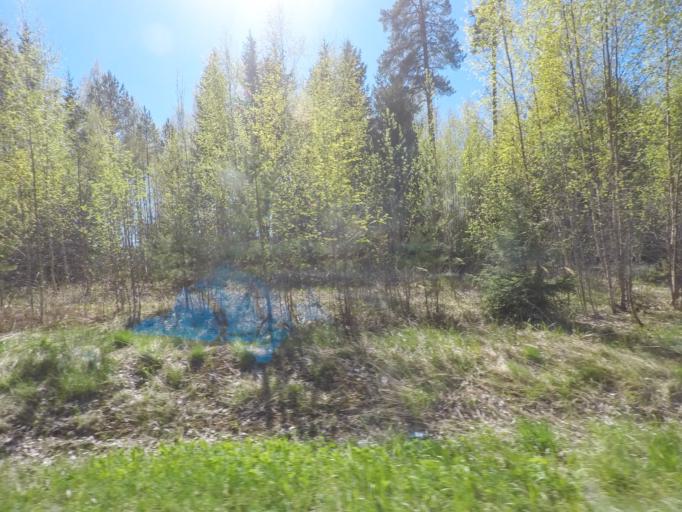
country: FI
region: Uusimaa
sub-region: Helsinki
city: Sammatti
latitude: 60.3336
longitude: 23.8046
